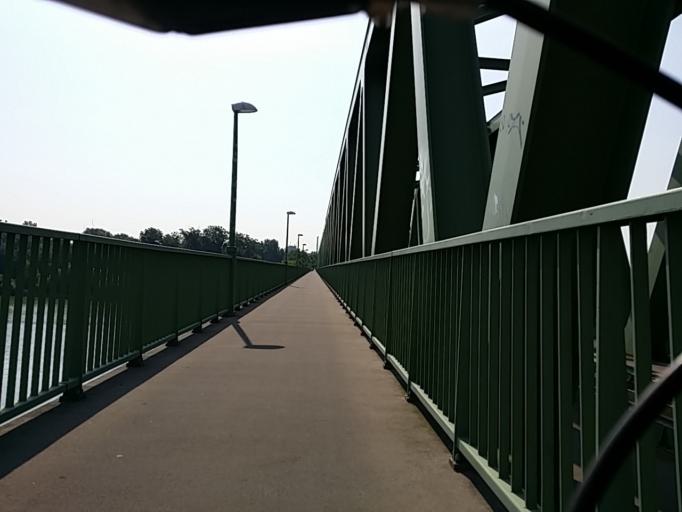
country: HU
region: Budapest
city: Budapest IV. keruelet
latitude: 47.5629
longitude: 19.0682
